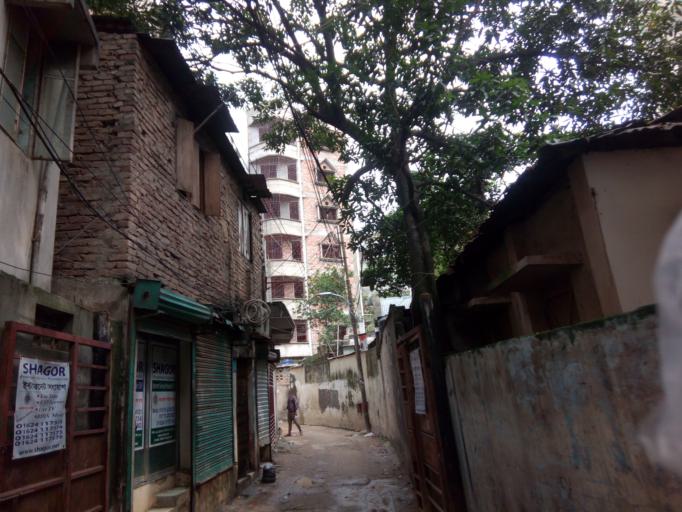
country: BD
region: Dhaka
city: Azimpur
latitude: 23.7417
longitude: 90.3678
